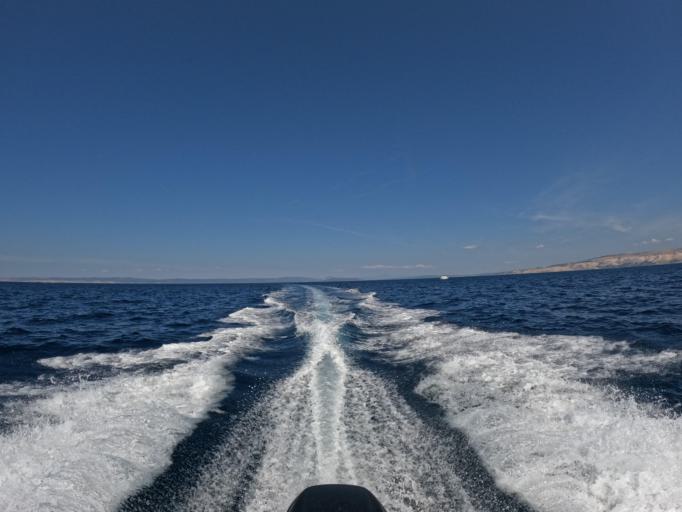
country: HR
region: Primorsko-Goranska
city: Lopar
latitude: 44.8717
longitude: 14.6693
